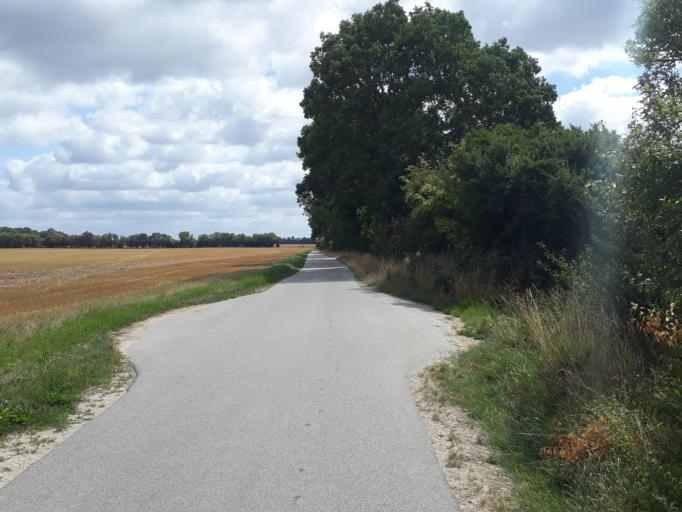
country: DE
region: Mecklenburg-Vorpommern
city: Marlow
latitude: 54.2179
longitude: 12.5613
